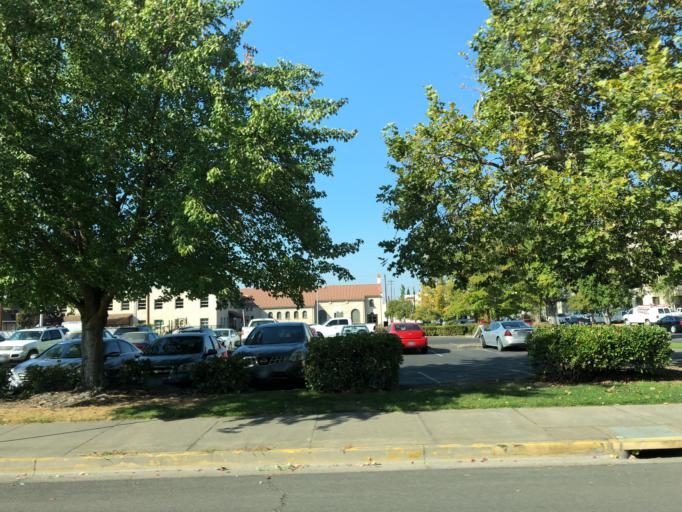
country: US
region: Oregon
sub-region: Jackson County
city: Medford
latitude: 42.3225
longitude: -122.8787
